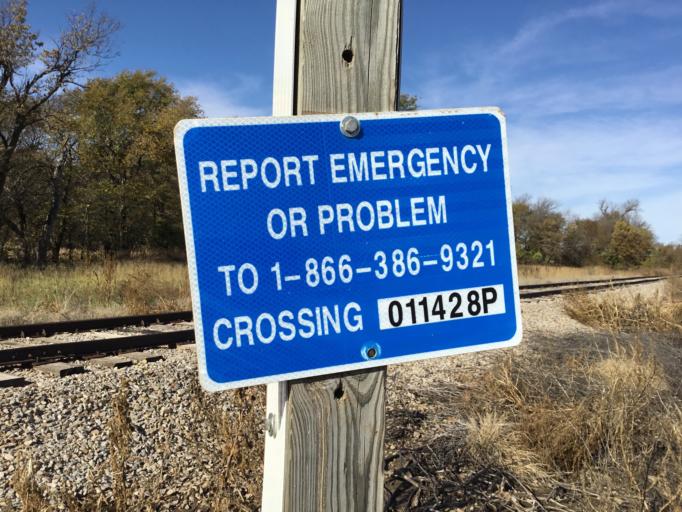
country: US
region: Kansas
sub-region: Lincoln County
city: Lincoln
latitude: 38.9815
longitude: -98.0588
